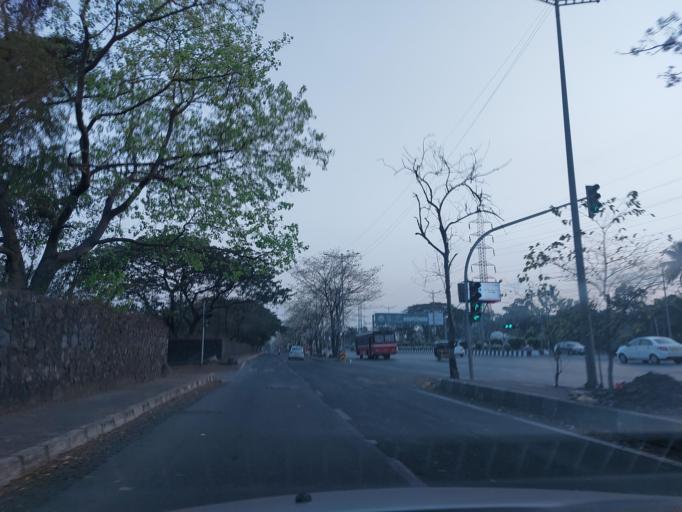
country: IN
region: Maharashtra
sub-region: Mumbai Suburban
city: Powai
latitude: 19.1008
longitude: 72.9293
